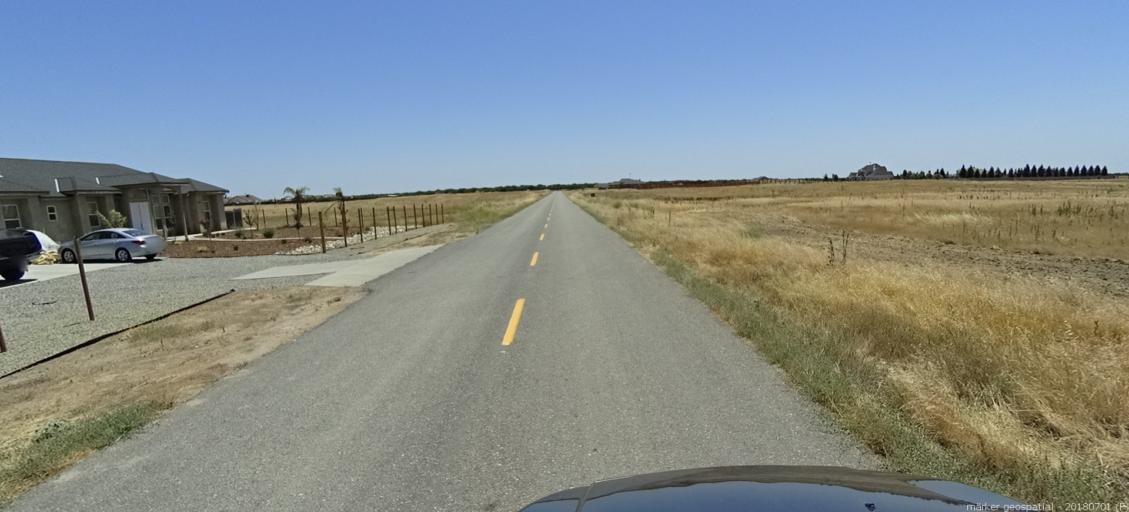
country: US
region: California
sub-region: Madera County
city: Madera Acres
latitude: 37.0599
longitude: -120.0134
